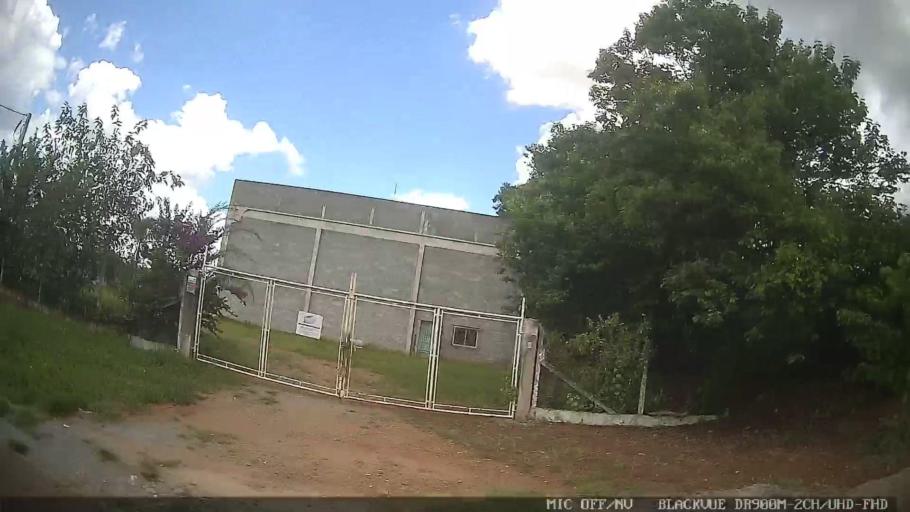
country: BR
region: Sao Paulo
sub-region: Braganca Paulista
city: Braganca Paulista
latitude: -22.9887
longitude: -46.4851
